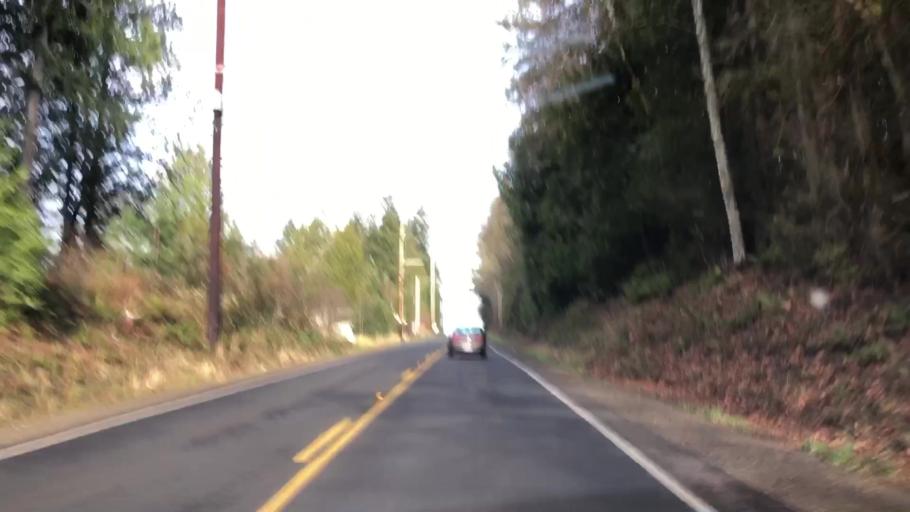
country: US
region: Washington
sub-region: Kitsap County
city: Kingston
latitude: 47.7902
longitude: -122.5414
